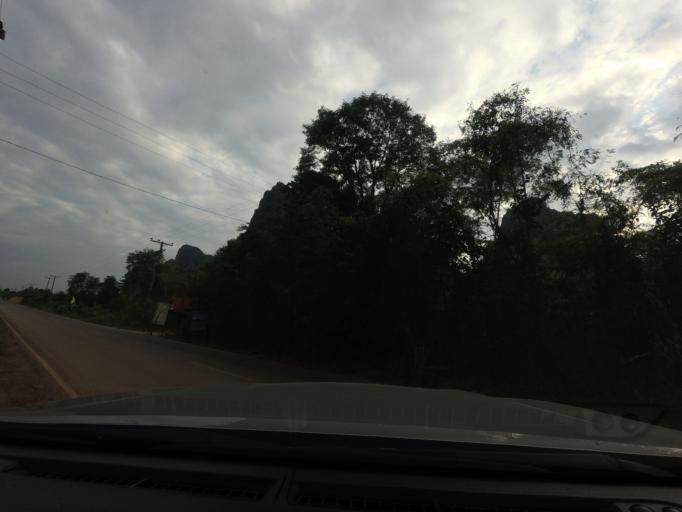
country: TH
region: Phitsanulok
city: Noen Maprang
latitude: 16.5772
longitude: 100.6826
